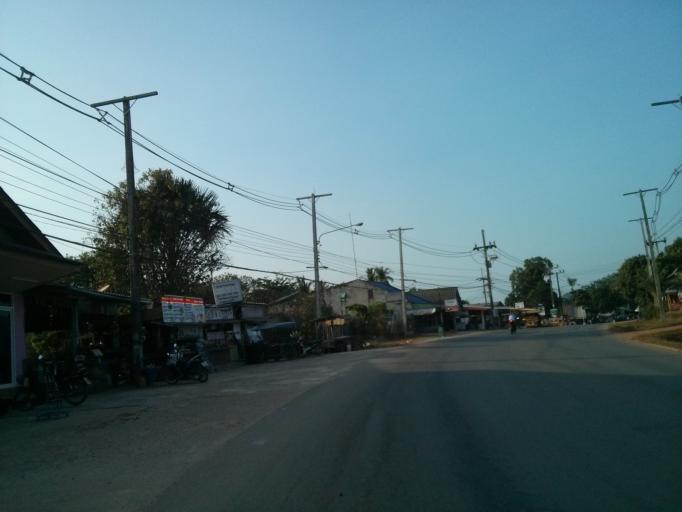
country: TH
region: Krabi
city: Saladan
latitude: 7.5941
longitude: 99.0351
